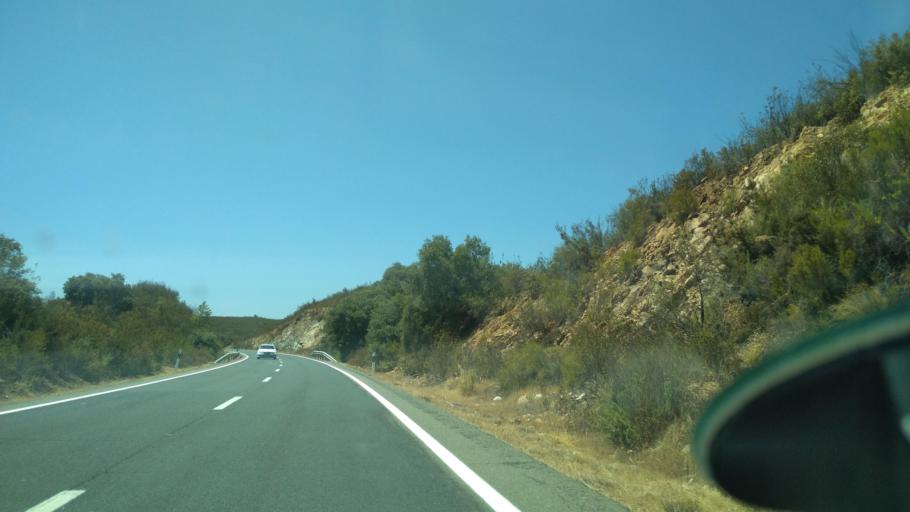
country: ES
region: Andalusia
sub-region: Provincia de Huelva
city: Aracena
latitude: 37.8541
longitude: -6.5695
